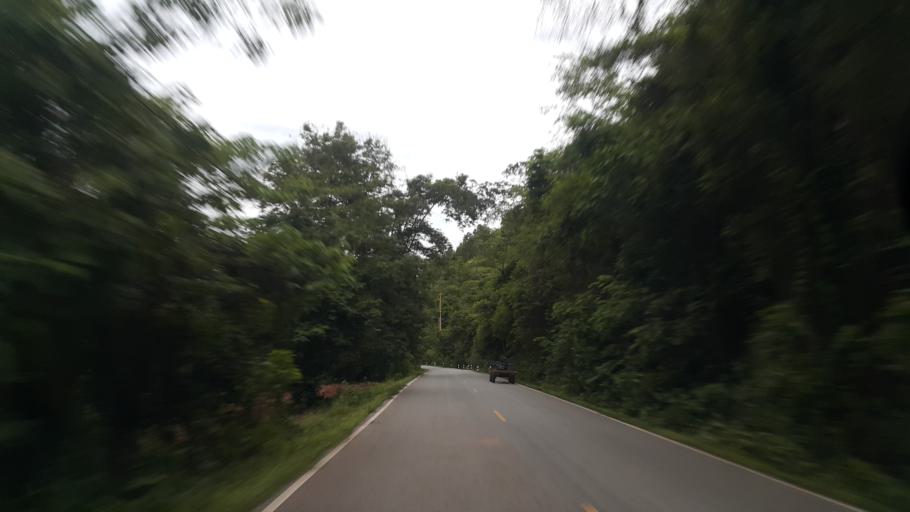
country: TH
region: Loei
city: Na Haeo
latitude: 17.5301
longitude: 101.1954
